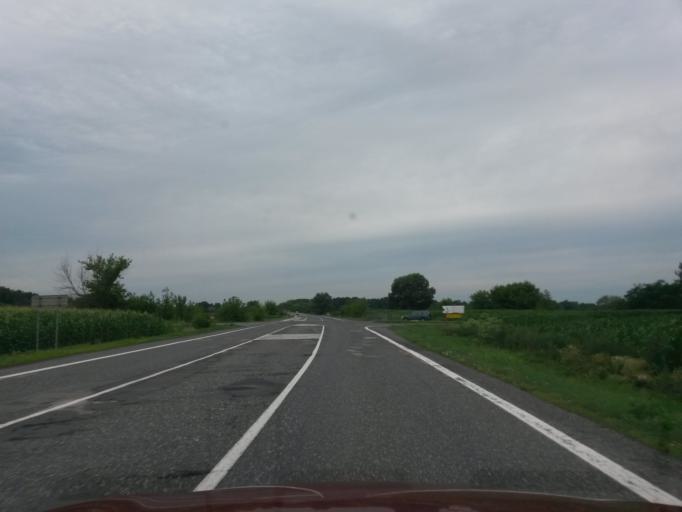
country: SK
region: Nitriansky
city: Zeliezovce
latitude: 48.1203
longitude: 18.6412
